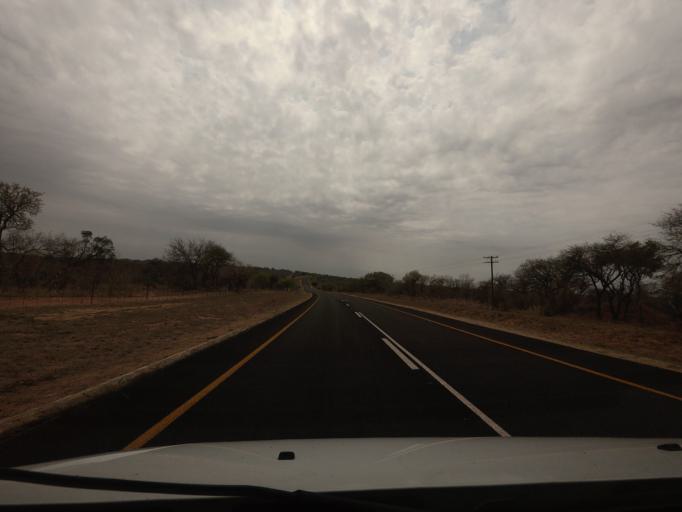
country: ZA
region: Limpopo
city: Thulamahashi
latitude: -24.5589
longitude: 31.1765
